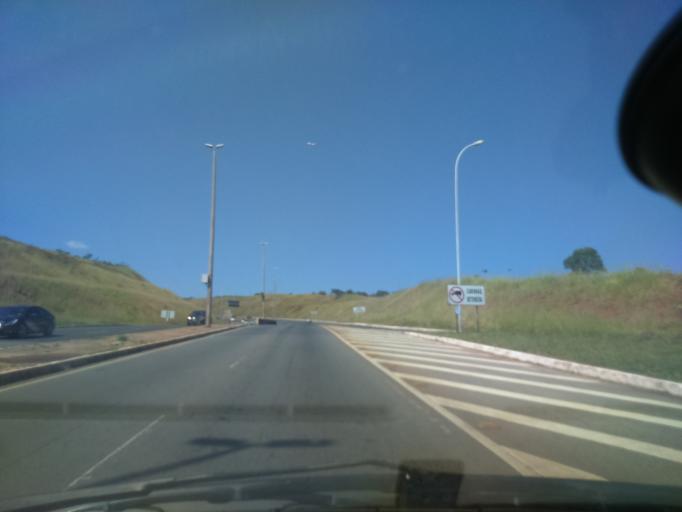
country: BR
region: Federal District
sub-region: Brasilia
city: Brasilia
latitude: -15.8358
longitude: -47.8249
